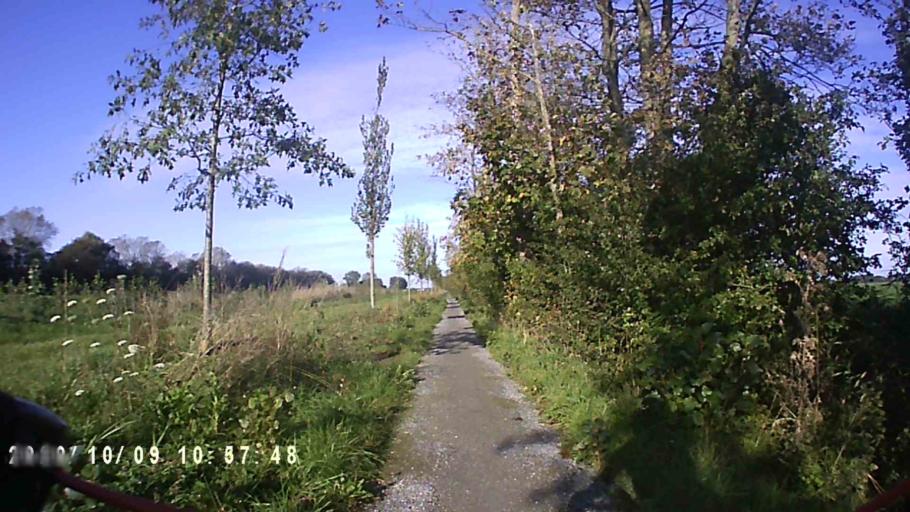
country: NL
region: Groningen
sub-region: Gemeente Groningen
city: Korrewegwijk
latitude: 53.2539
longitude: 6.5208
